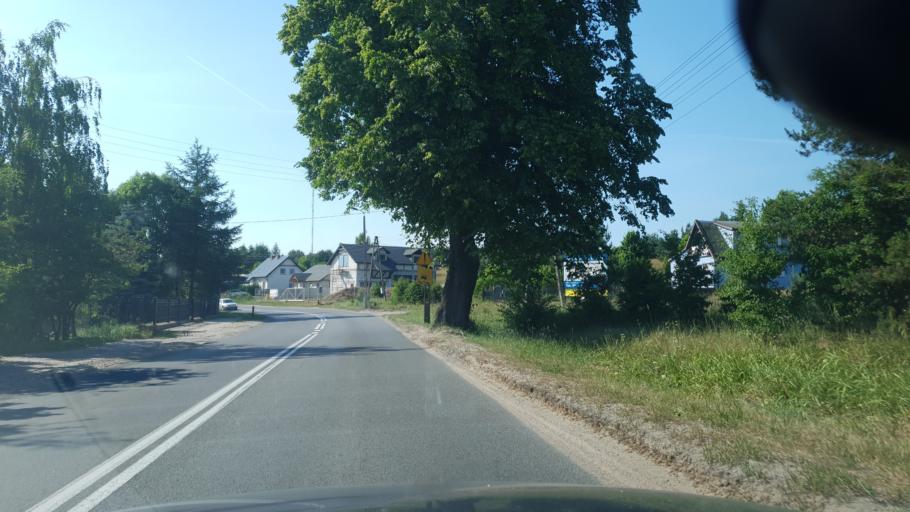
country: PL
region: Pomeranian Voivodeship
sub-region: Powiat kartuski
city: Chwaszczyno
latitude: 54.4410
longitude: 18.4559
